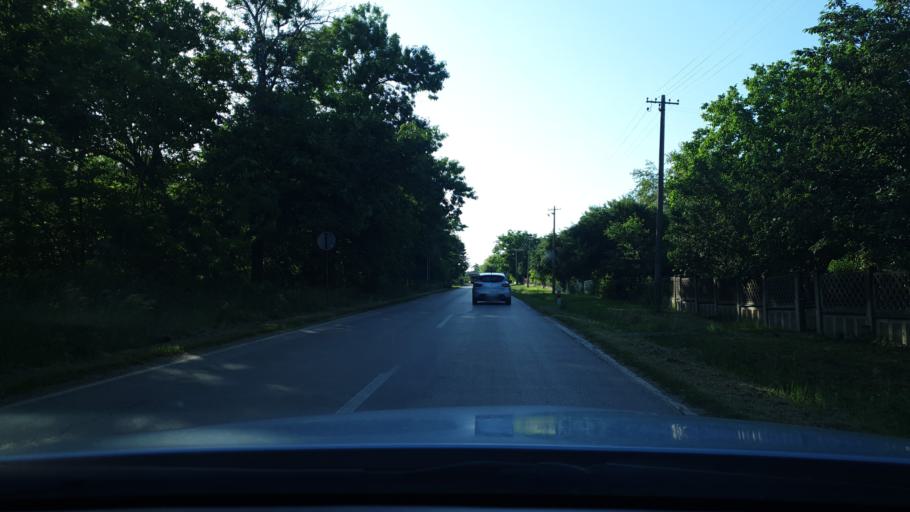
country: RS
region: Central Serbia
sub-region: Nisavski Okrug
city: Razanj
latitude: 43.6192
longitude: 21.5806
